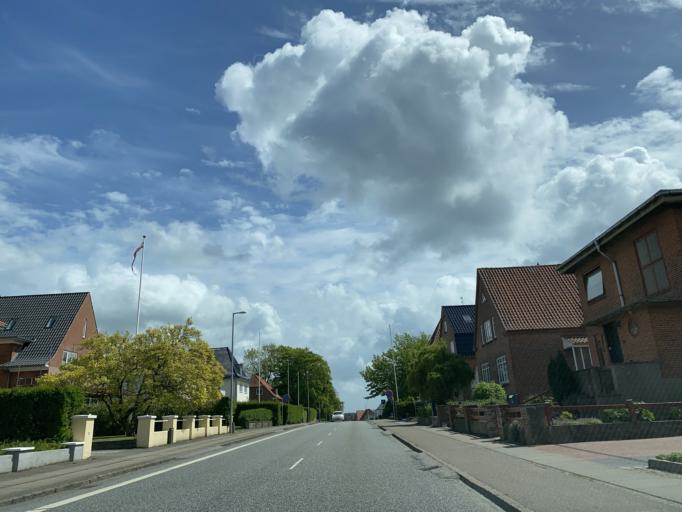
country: DK
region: South Denmark
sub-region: Sonderborg Kommune
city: Sonderborg
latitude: 54.9068
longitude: 9.7968
